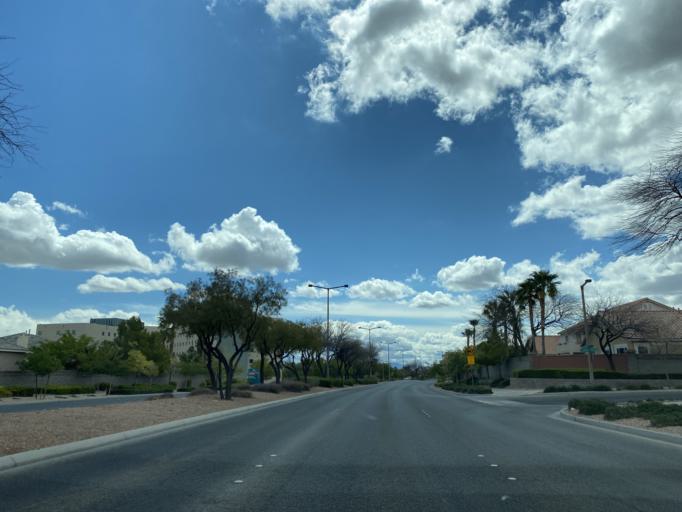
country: US
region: Nevada
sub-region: Clark County
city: Summerlin South
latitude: 36.1822
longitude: -115.3209
